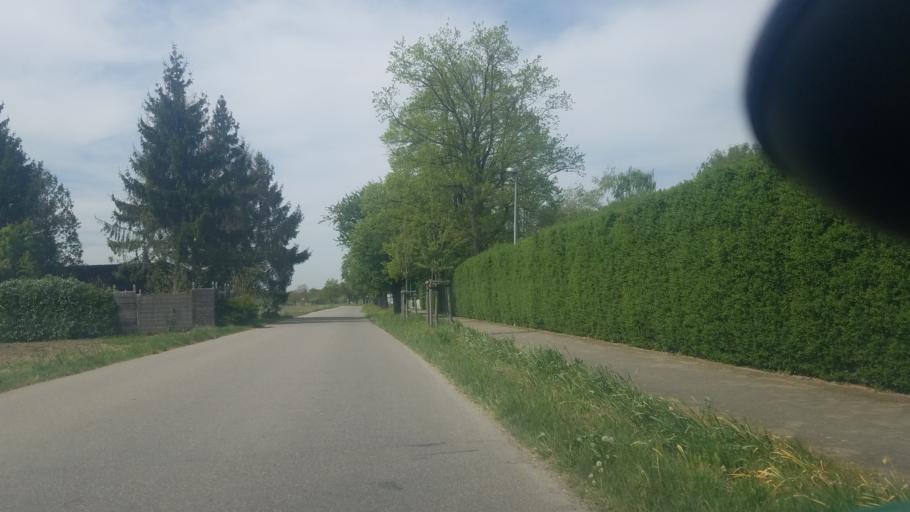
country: DE
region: Baden-Wuerttemberg
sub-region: Freiburg Region
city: Meissenheim
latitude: 48.4387
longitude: 7.7970
